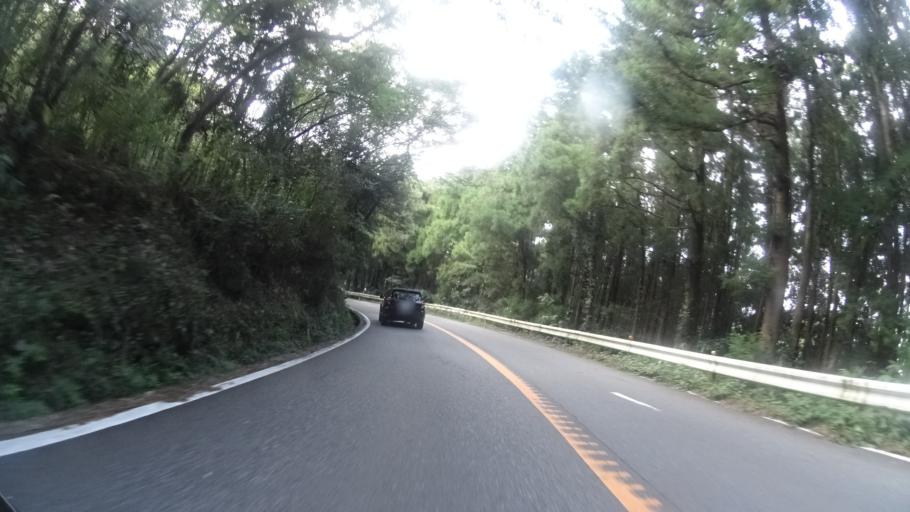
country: JP
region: Oita
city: Beppu
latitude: 33.2883
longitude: 131.4576
